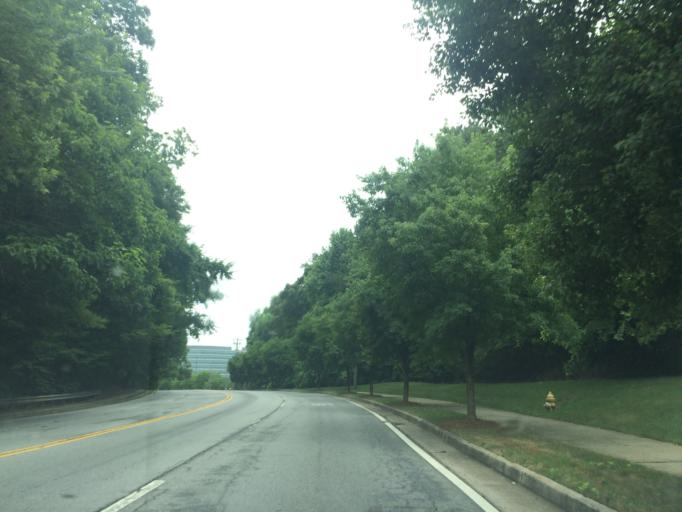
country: US
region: Georgia
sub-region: DeKalb County
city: Druid Hills
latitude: 33.8031
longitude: -84.3333
